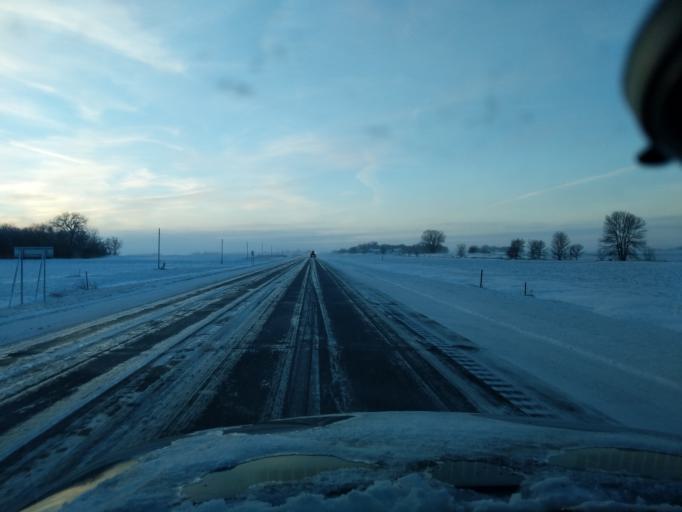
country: US
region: Minnesota
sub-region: Renville County
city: Renville
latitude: 44.7890
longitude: -95.3029
